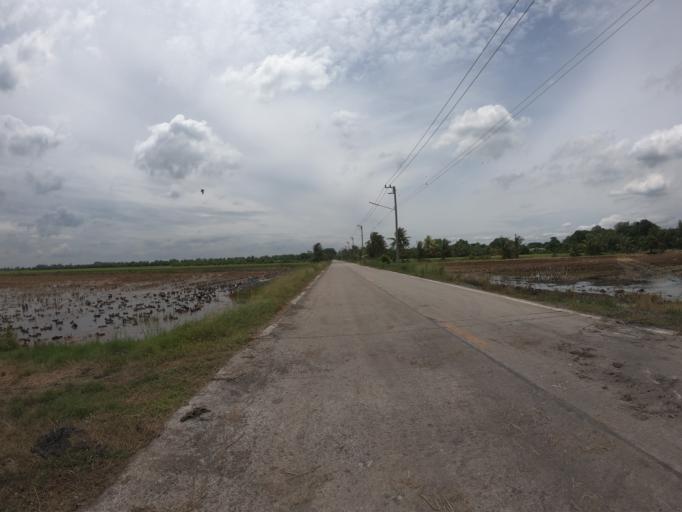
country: TH
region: Pathum Thani
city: Ban Lam Luk Ka
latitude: 14.0258
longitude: 100.8658
